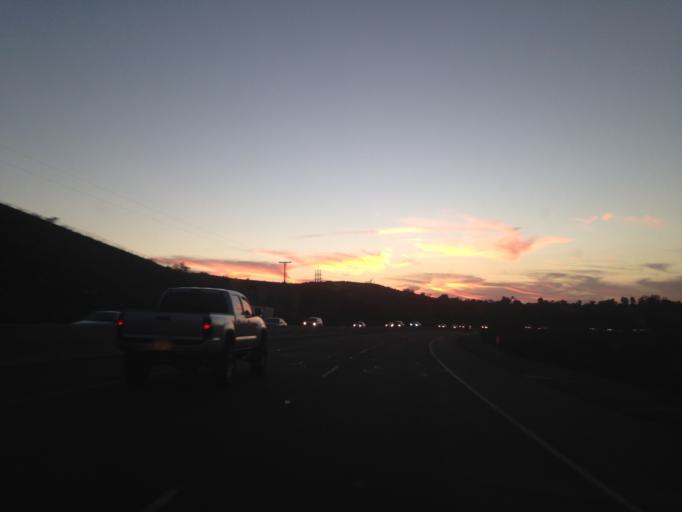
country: US
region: California
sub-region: San Diego County
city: Bonsall
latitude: 33.2542
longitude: -117.2420
